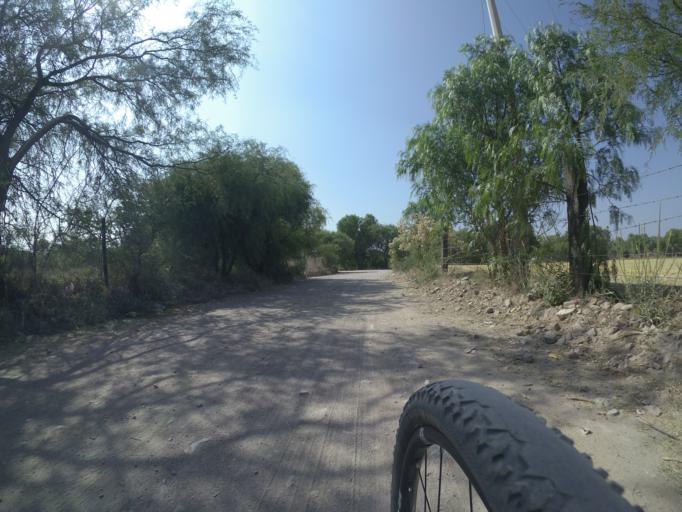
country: MX
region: Aguascalientes
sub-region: Jesus Maria
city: Paseos de las Haciendas [Fraccionamiento]
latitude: 22.0000
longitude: -102.3532
